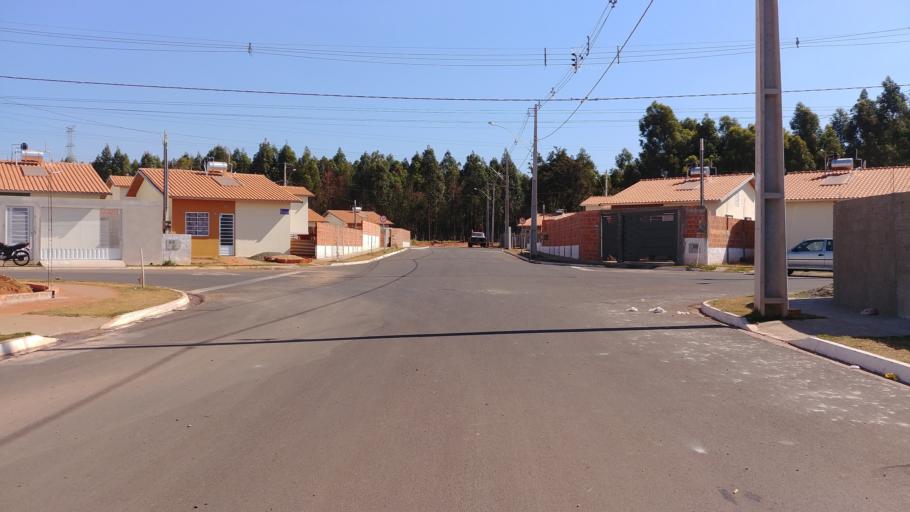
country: BR
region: Sao Paulo
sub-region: Paraguacu Paulista
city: Paraguacu Paulista
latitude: -22.4451
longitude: -50.5884
